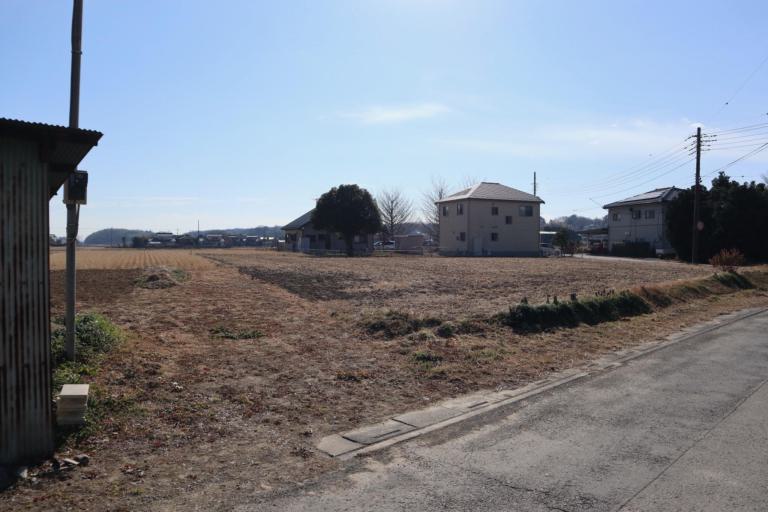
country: JP
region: Saitama
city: Fukiage-fujimi
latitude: 36.0784
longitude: 139.4290
